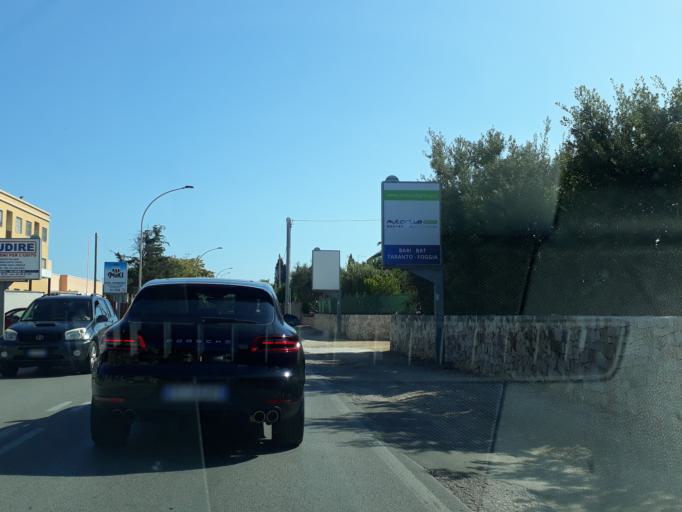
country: IT
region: Apulia
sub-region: Provincia di Bari
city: Monopoli
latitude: 40.9451
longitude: 17.2971
